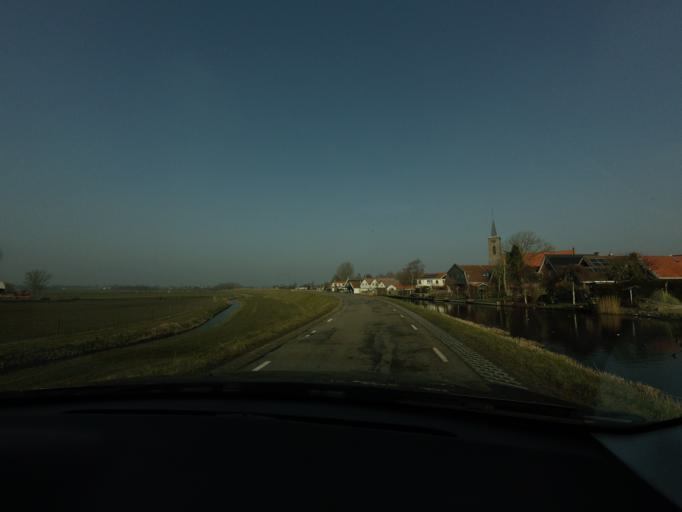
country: NL
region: North Holland
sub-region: Gemeente Heerhugowaard
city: Heerhugowaard
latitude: 52.6253
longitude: 4.8891
